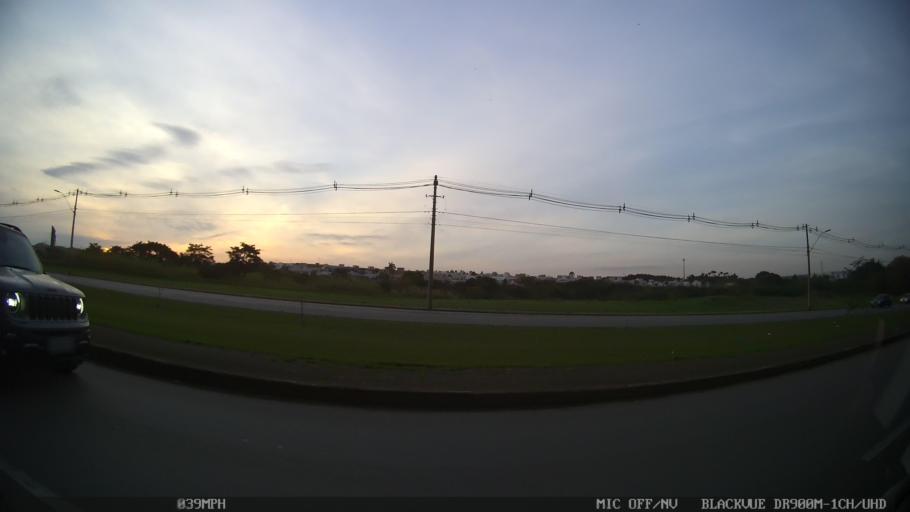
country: BR
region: Sao Paulo
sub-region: Limeira
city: Limeira
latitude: -22.5477
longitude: -47.4263
